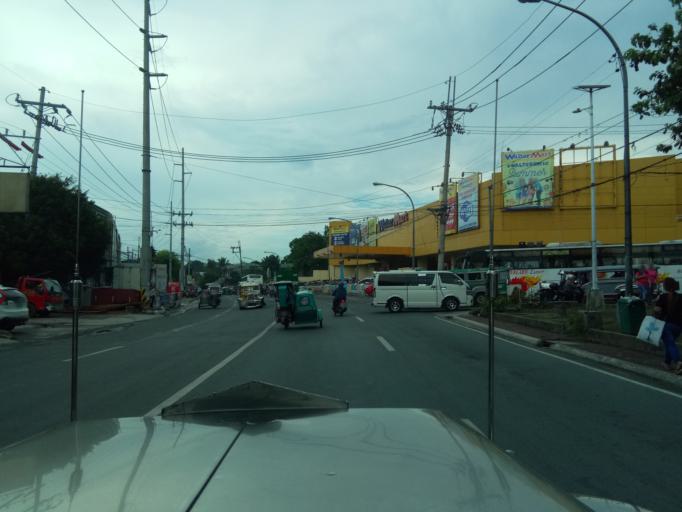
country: PH
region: Calabarzon
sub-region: Province of Cavite
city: Aliang
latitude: 14.2812
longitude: 120.8707
